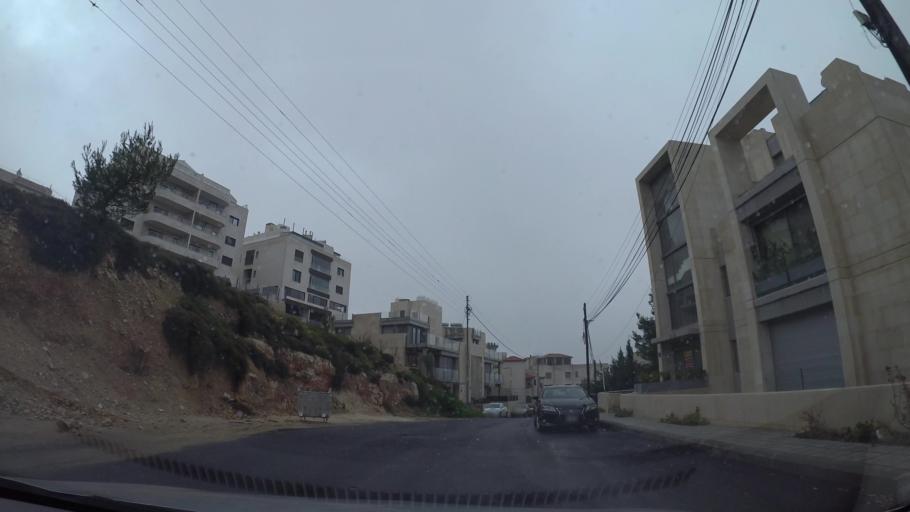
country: JO
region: Amman
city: Wadi as Sir
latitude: 32.0000
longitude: 35.8181
